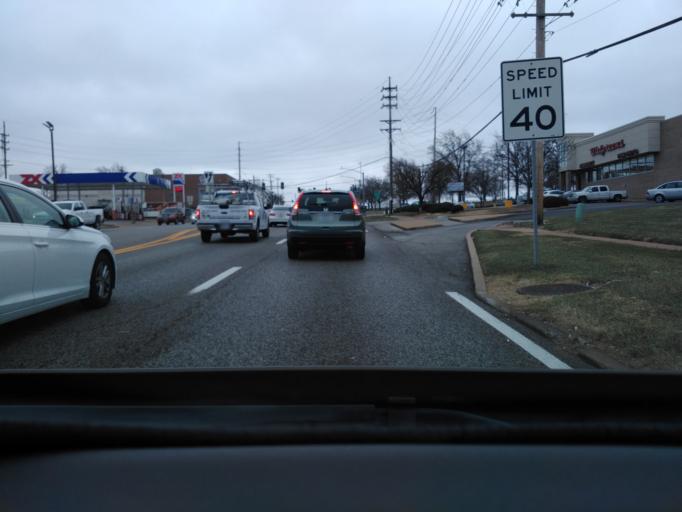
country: US
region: Missouri
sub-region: Saint Louis County
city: Mehlville
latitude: 38.5005
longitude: -90.3333
